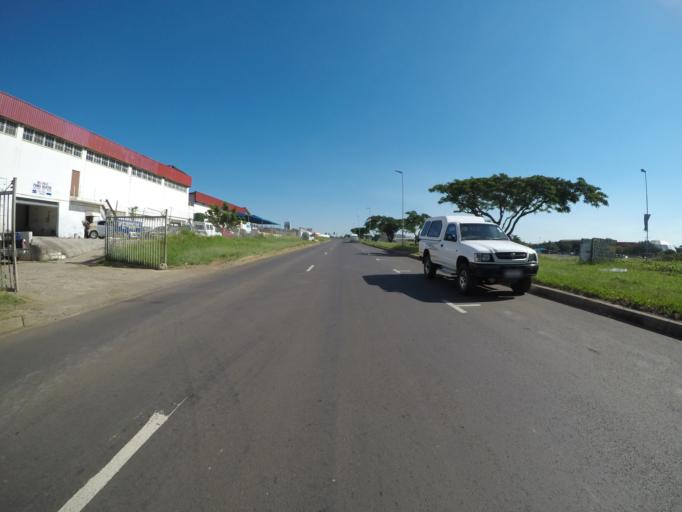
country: ZA
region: KwaZulu-Natal
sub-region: uThungulu District Municipality
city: Empangeni
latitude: -28.7727
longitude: 31.9021
